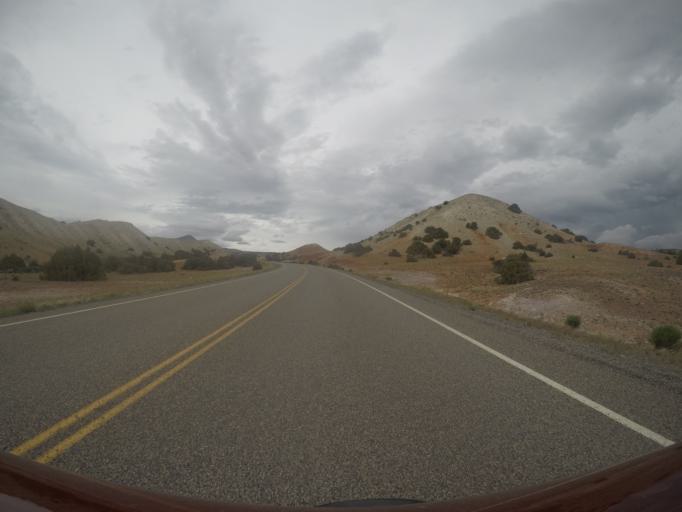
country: US
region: Wyoming
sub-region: Big Horn County
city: Lovell
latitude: 44.9729
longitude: -108.2629
